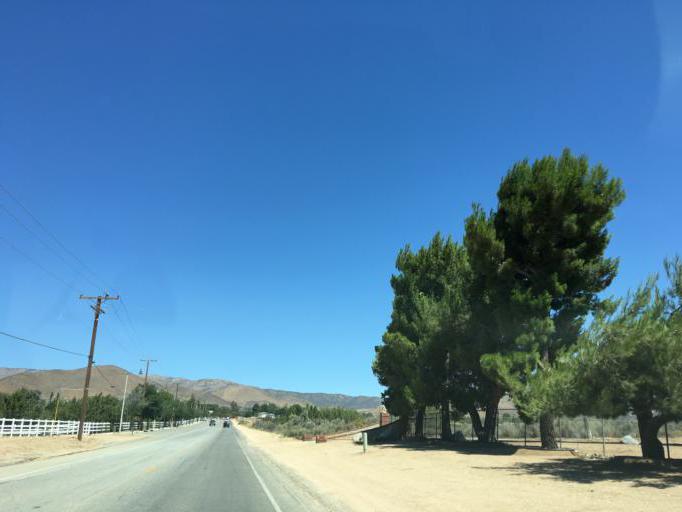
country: US
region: California
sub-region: Los Angeles County
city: Acton
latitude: 34.4764
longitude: -118.1976
